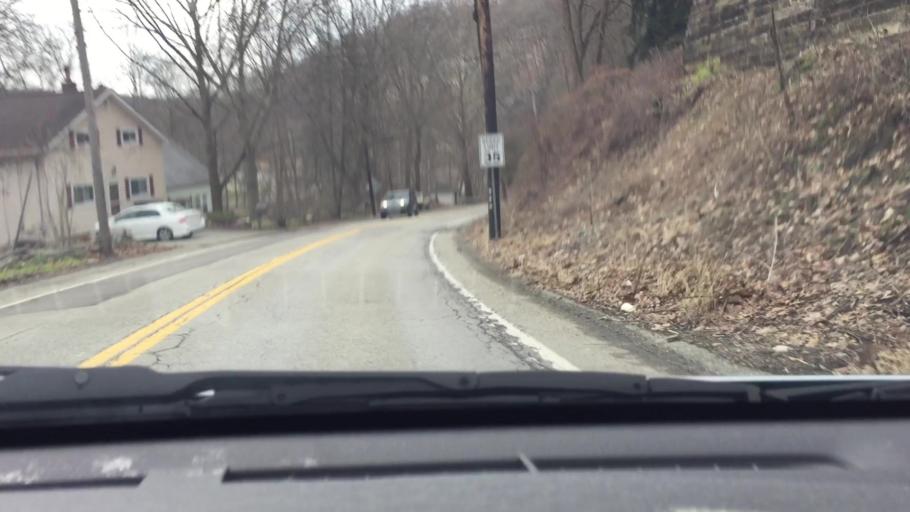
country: US
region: Pennsylvania
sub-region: Allegheny County
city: Allison Park
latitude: 40.5624
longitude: -79.9658
